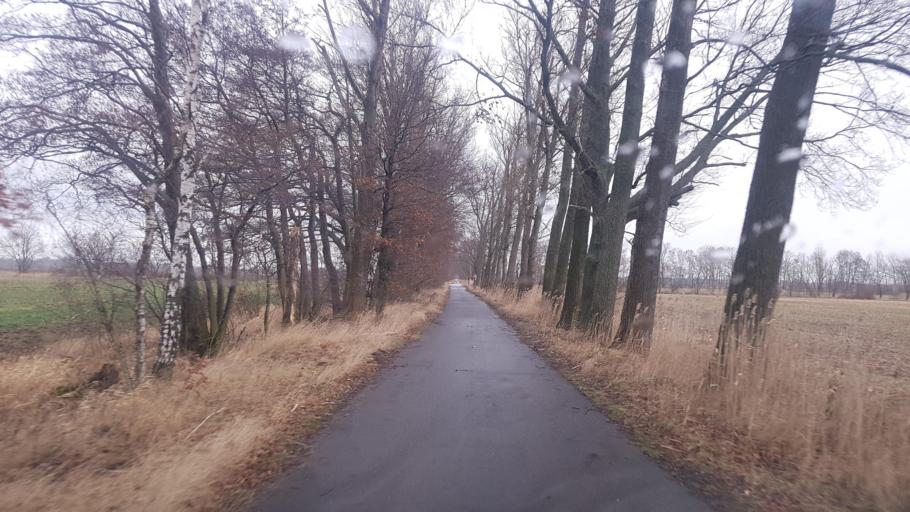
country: DE
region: Brandenburg
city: Grossthiemig
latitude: 51.4107
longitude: 13.6492
